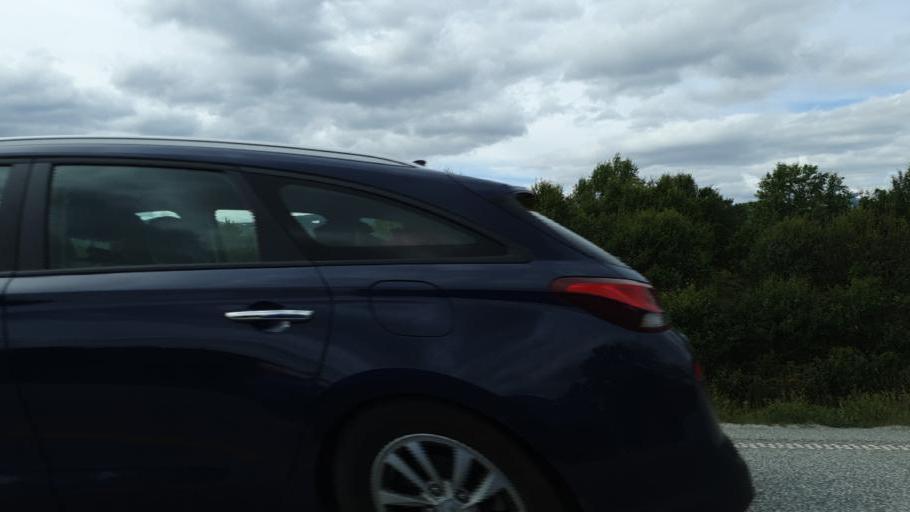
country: NO
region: Oppland
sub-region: Dovre
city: Dovre
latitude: 62.1360
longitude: 9.3157
